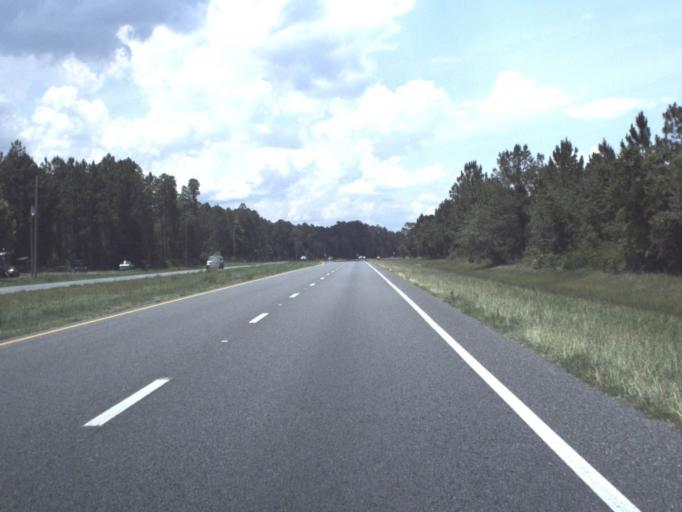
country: US
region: Florida
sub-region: Putnam County
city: Palatka
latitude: 29.8053
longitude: -81.6567
